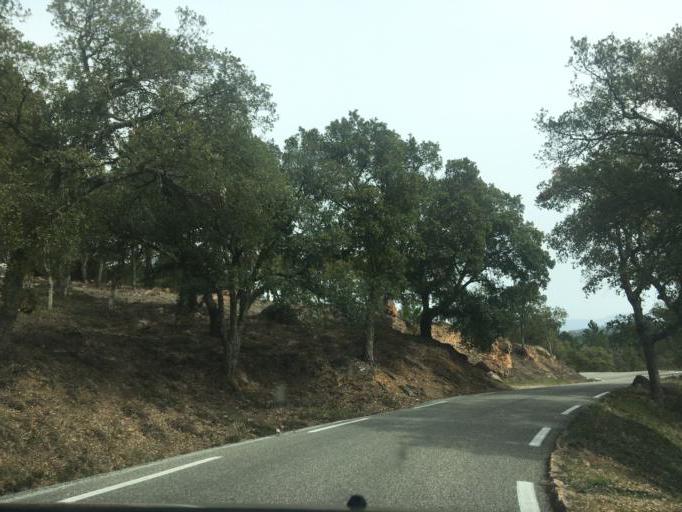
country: FR
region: Provence-Alpes-Cote d'Azur
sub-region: Departement du Var
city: Bagnols-en-Foret
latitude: 43.5259
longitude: 6.6516
